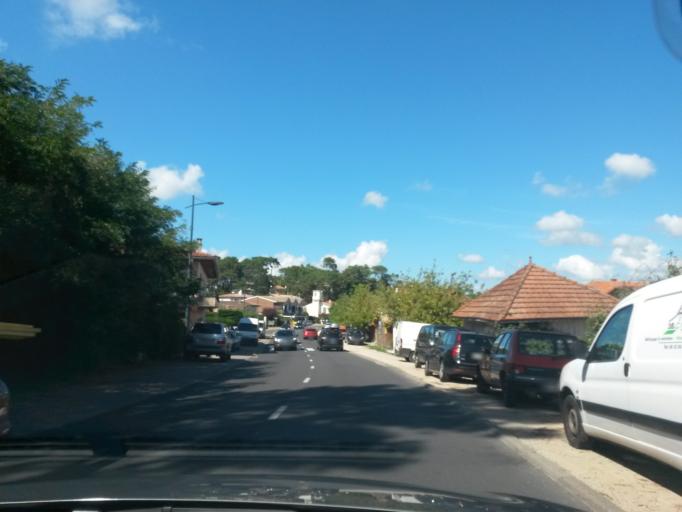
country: FR
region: Aquitaine
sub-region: Departement de la Gironde
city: Arcachon
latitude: 44.6992
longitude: -1.2298
